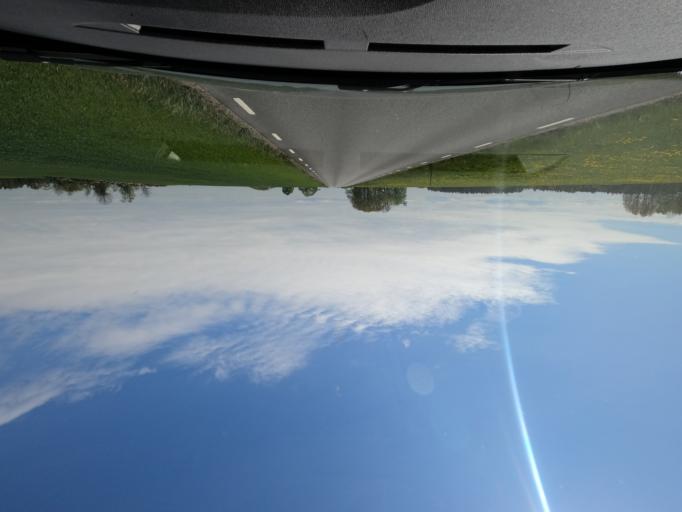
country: SE
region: Joenkoeping
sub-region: Varnamo Kommun
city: Bredaryd
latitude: 57.1453
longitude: 13.7203
